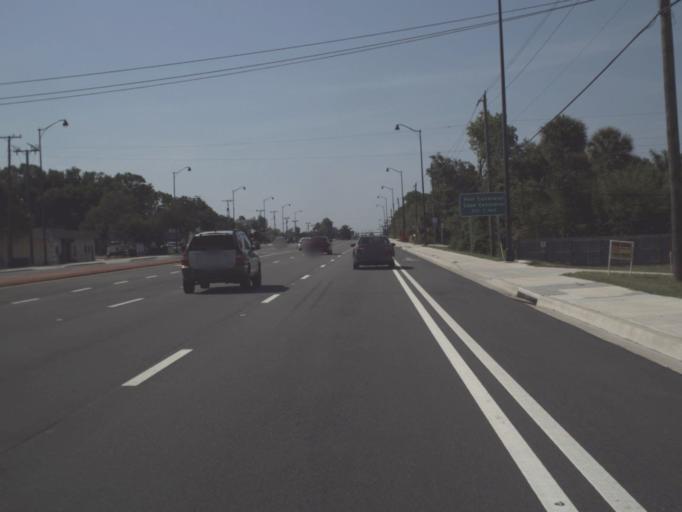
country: US
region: Florida
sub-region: Brevard County
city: Cocoa
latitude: 28.3853
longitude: -80.7431
